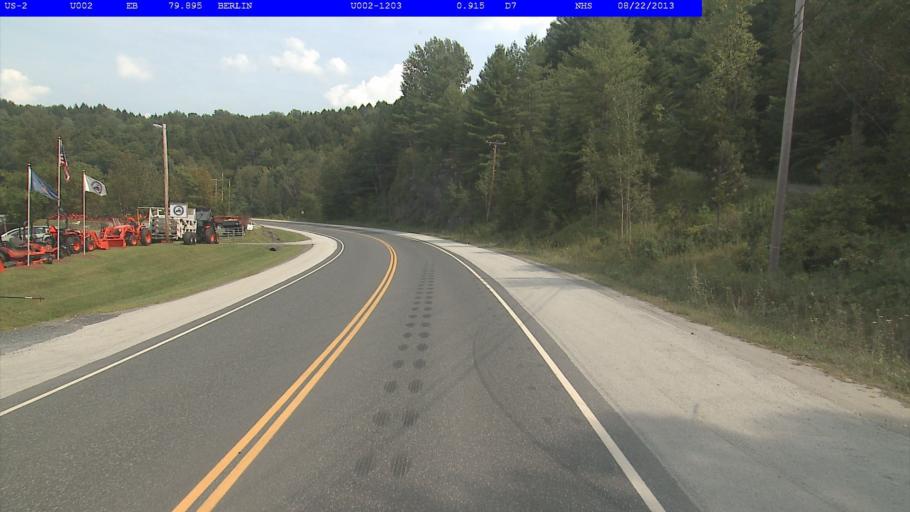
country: US
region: Vermont
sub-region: Washington County
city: Barre
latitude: 44.2373
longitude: -72.5265
